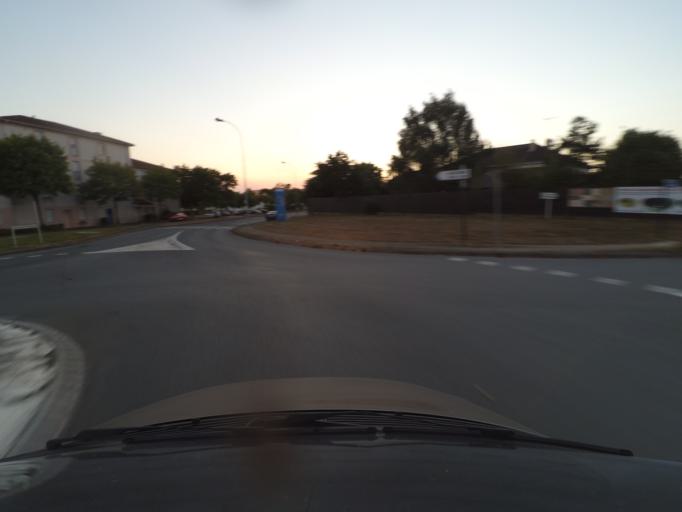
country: FR
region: Pays de la Loire
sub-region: Departement de la Vendee
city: La Roche-sur-Yon
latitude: 46.6527
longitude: -1.4414
